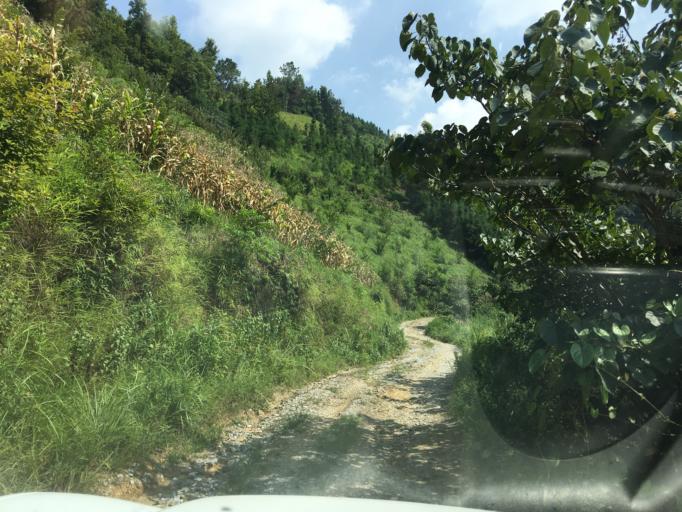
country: CN
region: Guangxi Zhuangzu Zizhiqu
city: Xinzhou
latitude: 24.9890
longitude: 105.7388
